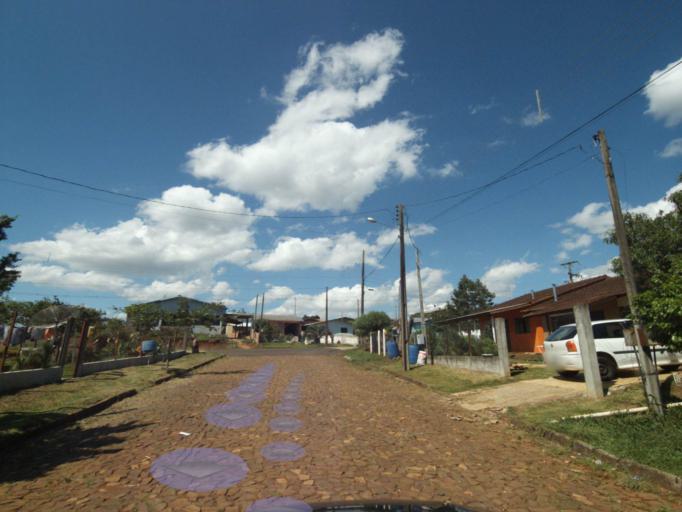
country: BR
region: Parana
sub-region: Coronel Vivida
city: Coronel Vivida
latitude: -26.1477
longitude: -52.3841
